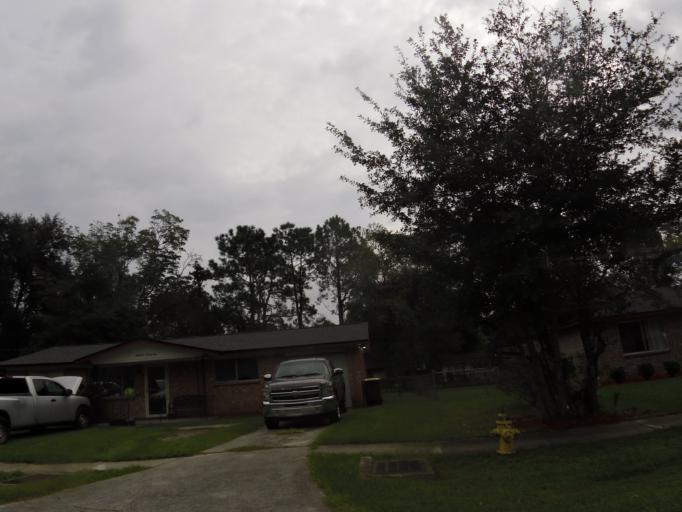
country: US
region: Florida
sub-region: Clay County
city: Bellair-Meadowbrook Terrace
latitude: 30.2514
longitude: -81.7306
